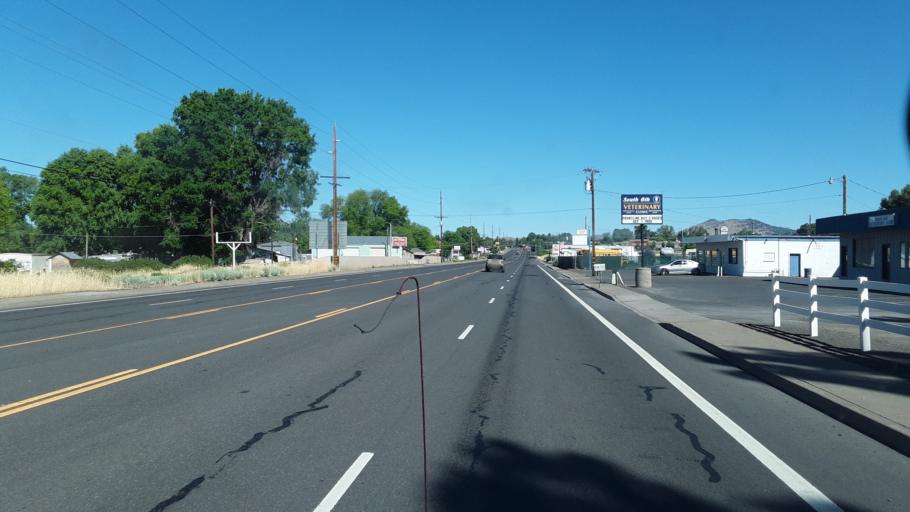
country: US
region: Oregon
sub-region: Klamath County
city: Altamont
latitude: 42.2004
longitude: -121.7043
